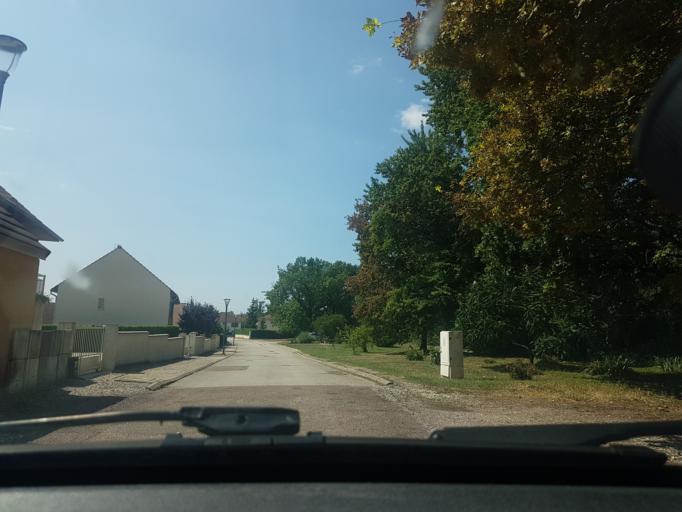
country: FR
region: Bourgogne
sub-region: Departement de Saone-et-Loire
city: Chagny
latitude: 46.9021
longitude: 4.7650
